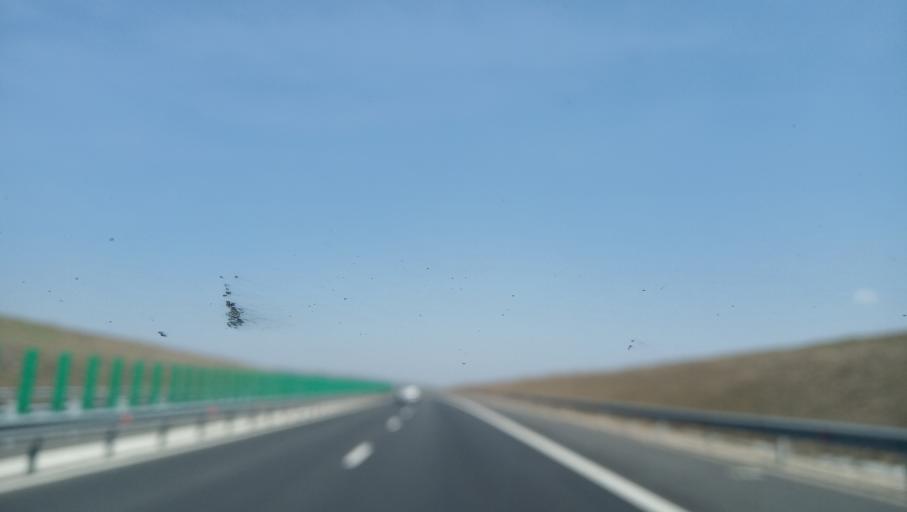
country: RO
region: Alba
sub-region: Comuna Unirea
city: Unirea
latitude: 46.3946
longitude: 23.7887
